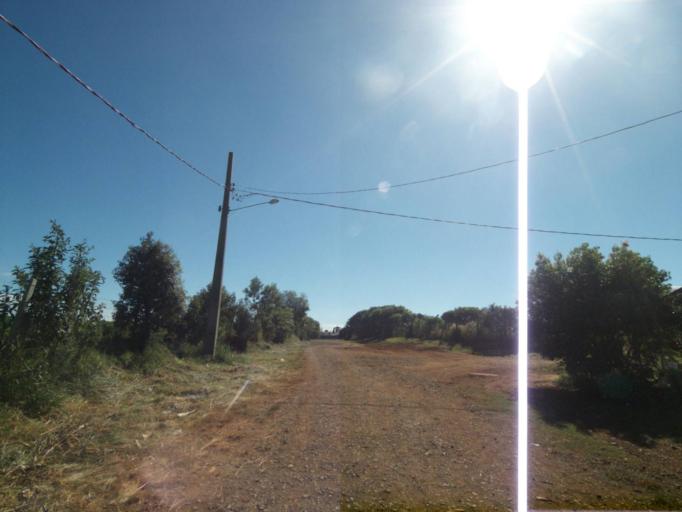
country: BR
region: Parana
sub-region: Pinhao
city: Pinhao
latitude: -25.8341
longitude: -52.0334
